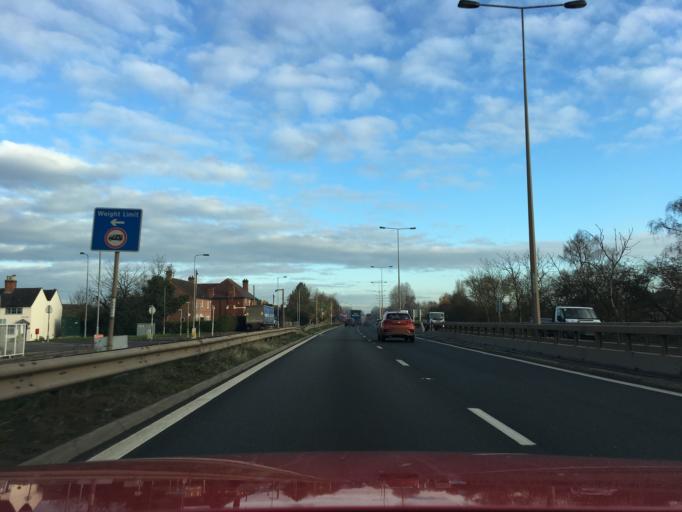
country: GB
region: England
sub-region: Staffordshire
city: Alrewas
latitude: 52.7311
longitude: -1.7406
